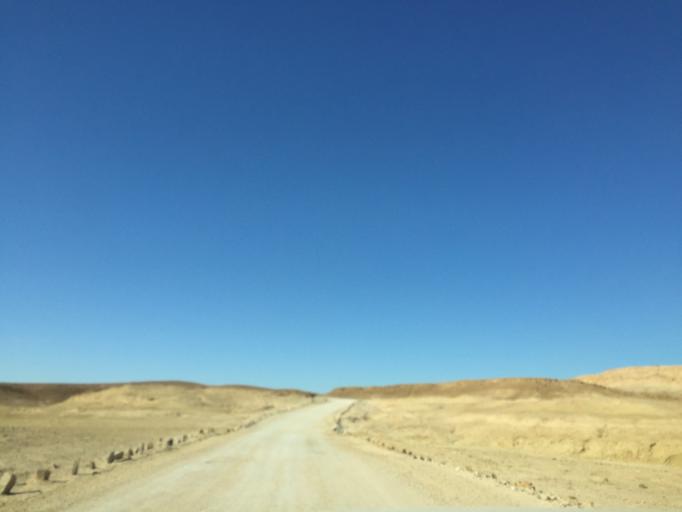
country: IL
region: Southern District
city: Mitzpe Ramon
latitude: 30.6111
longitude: 34.9351
